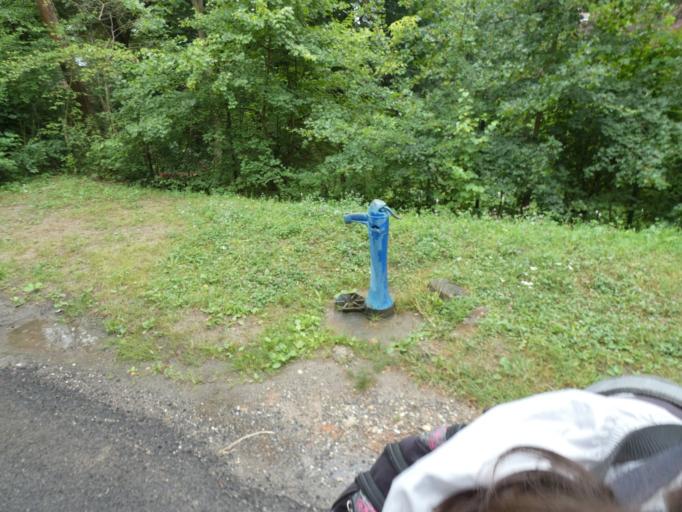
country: HU
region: Pest
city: Szob
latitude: 47.8107
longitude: 18.9020
